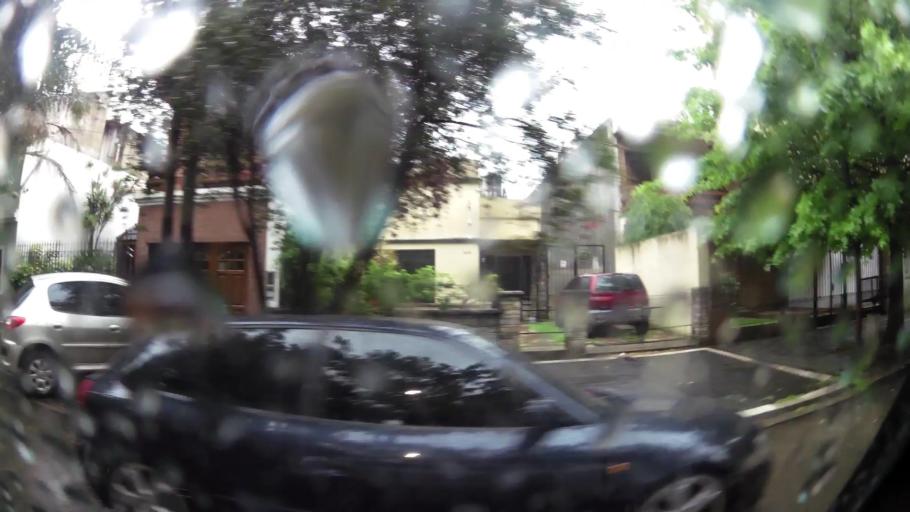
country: AR
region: Buenos Aires
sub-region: Partido de Lanus
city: Lanus
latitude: -34.7109
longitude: -58.3946
